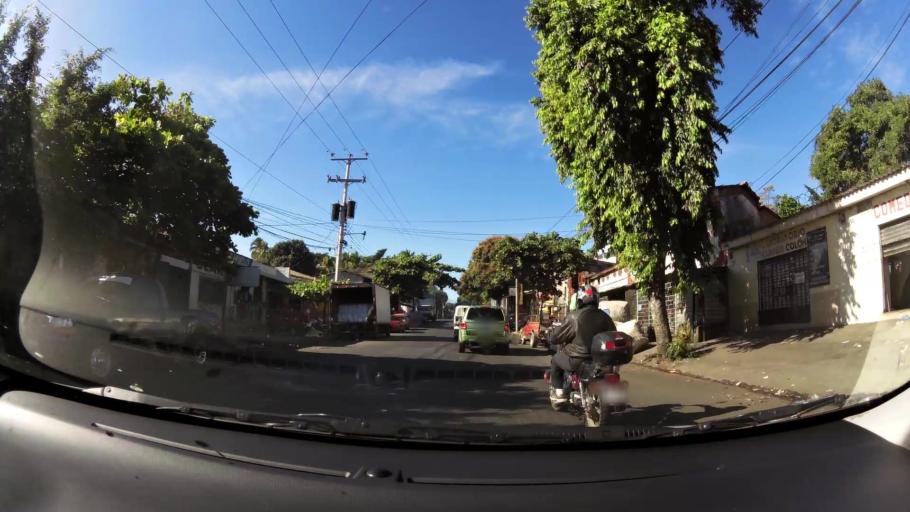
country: SV
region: Santa Ana
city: Santa Ana
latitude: 13.9884
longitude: -89.5657
